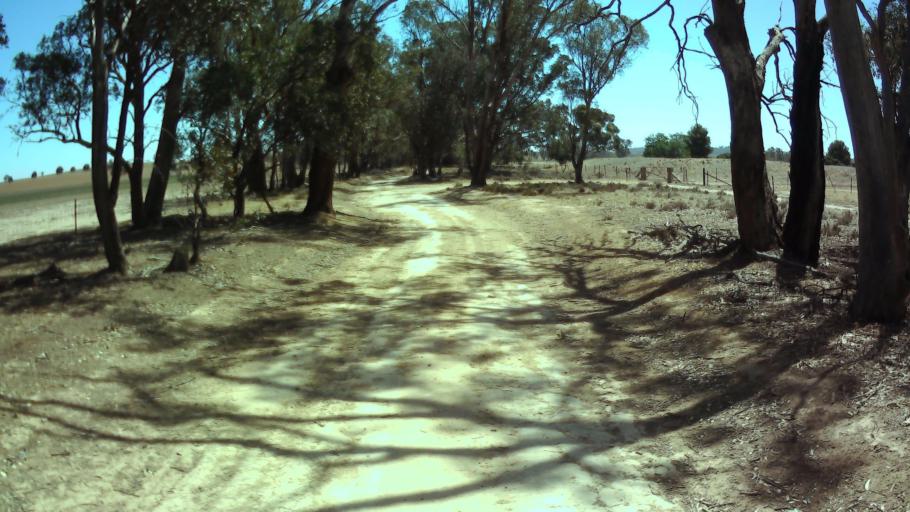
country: AU
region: New South Wales
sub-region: Weddin
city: Grenfell
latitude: -33.9924
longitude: 148.1636
